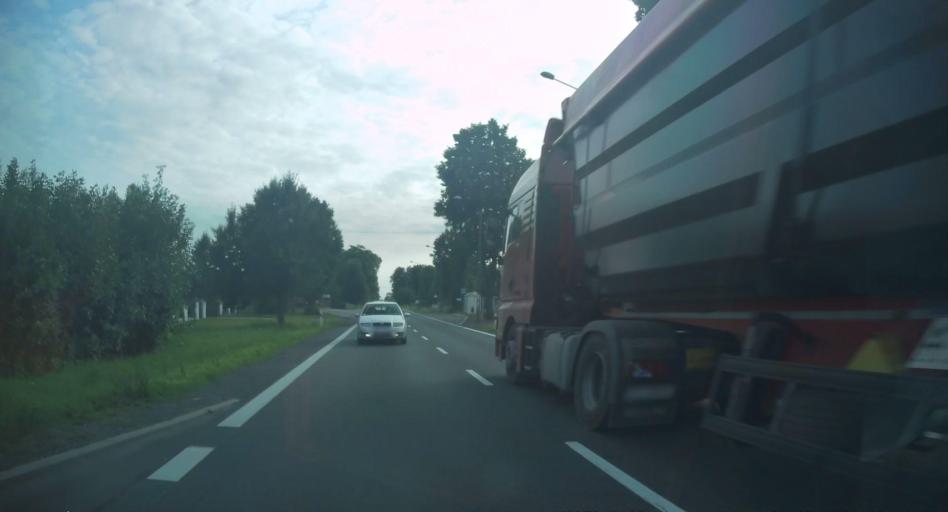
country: PL
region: Silesian Voivodeship
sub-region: Powiat czestochowski
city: Rudniki
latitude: 50.8913
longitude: 19.2695
